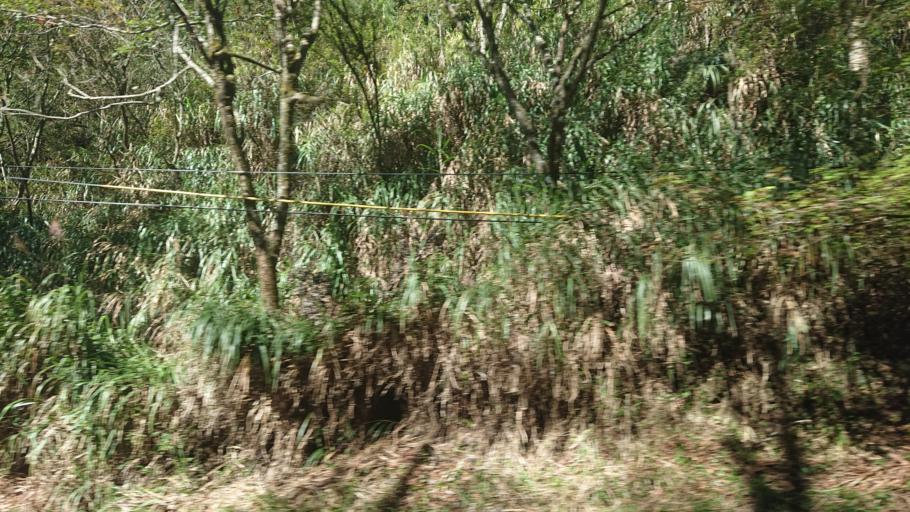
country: TW
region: Taiwan
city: Lugu
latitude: 23.4919
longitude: 120.7926
